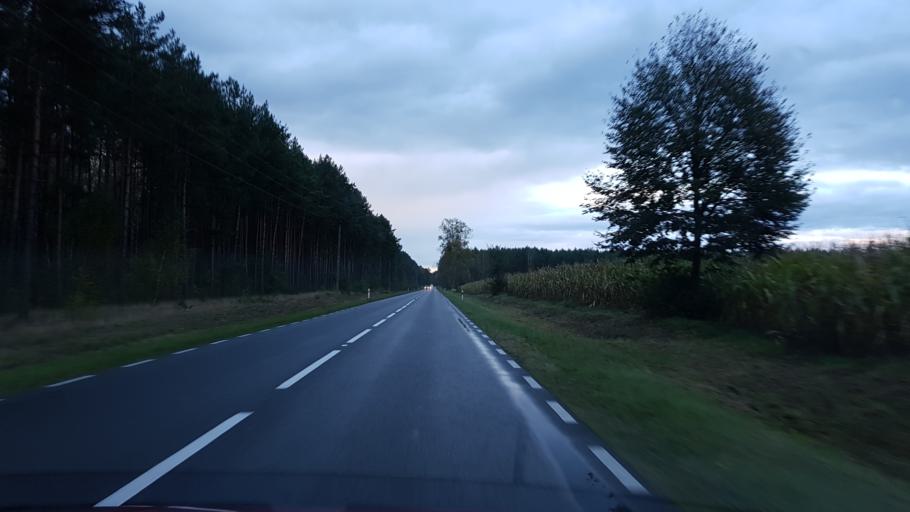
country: PL
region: Greater Poland Voivodeship
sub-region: Powiat zlotowski
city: Tarnowka
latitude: 53.2438
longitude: 16.8888
